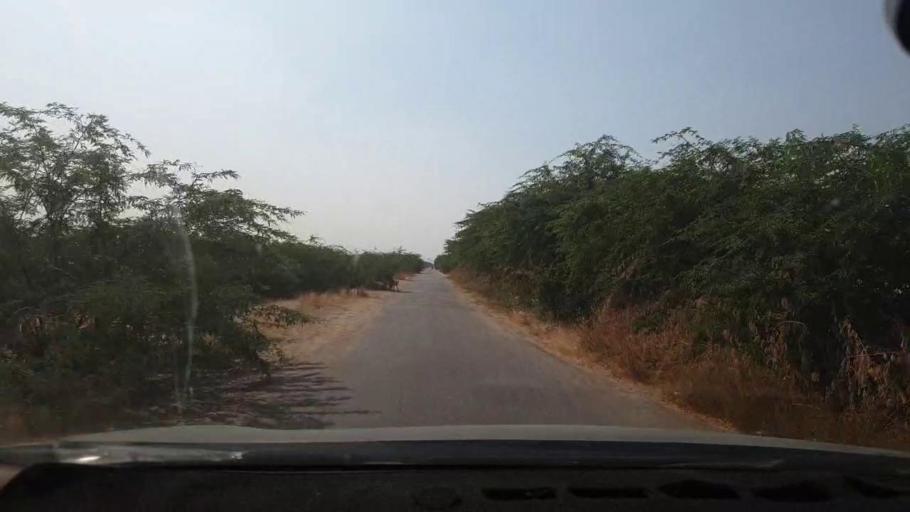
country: PK
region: Sindh
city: Malir Cantonment
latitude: 25.1197
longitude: 67.2157
